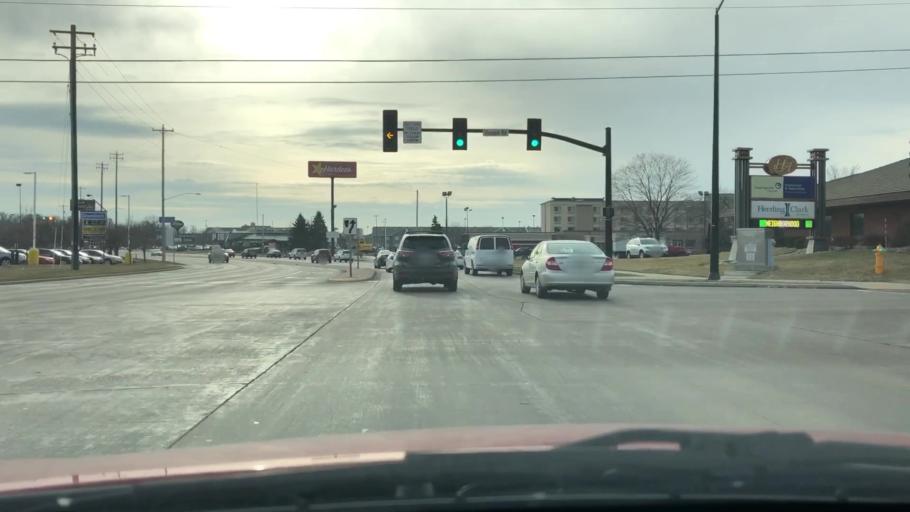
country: US
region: Wisconsin
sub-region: Brown County
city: Ashwaubenon
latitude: 44.4760
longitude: -88.0745
